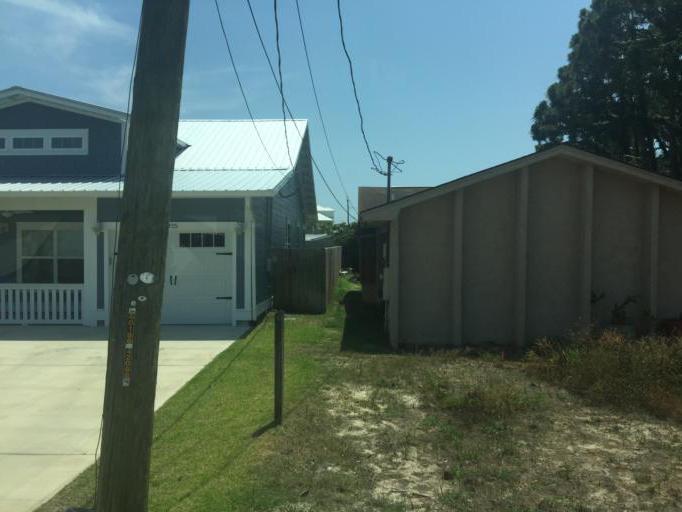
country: US
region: Florida
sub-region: Bay County
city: Lower Grand Lagoon
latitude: 30.1509
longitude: -85.7596
